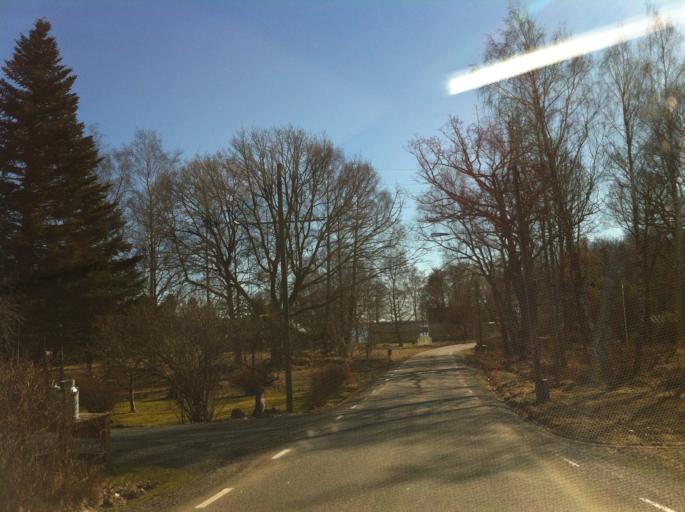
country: SE
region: Vaestra Goetaland
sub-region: Grastorps Kommun
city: Graestorp
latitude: 58.4498
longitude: 12.6174
